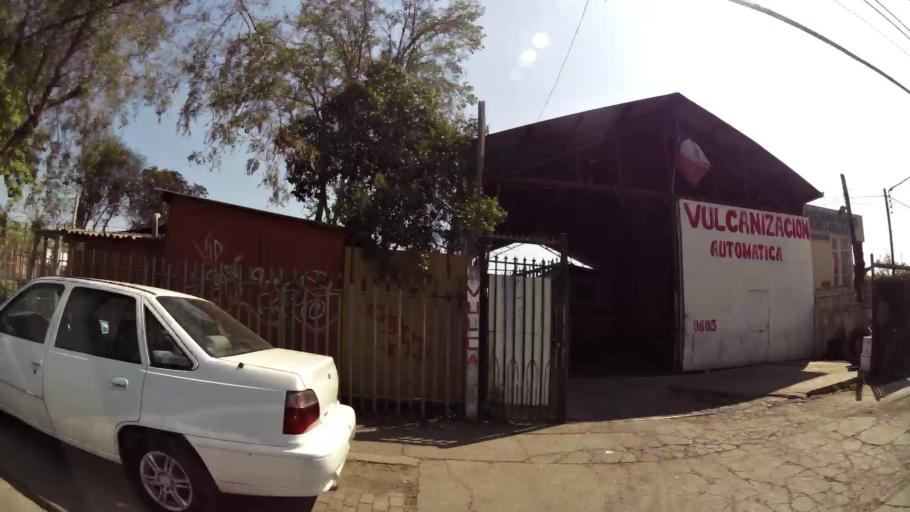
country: CL
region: Santiago Metropolitan
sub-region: Provincia de Santiago
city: La Pintana
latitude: -33.5459
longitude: -70.6037
